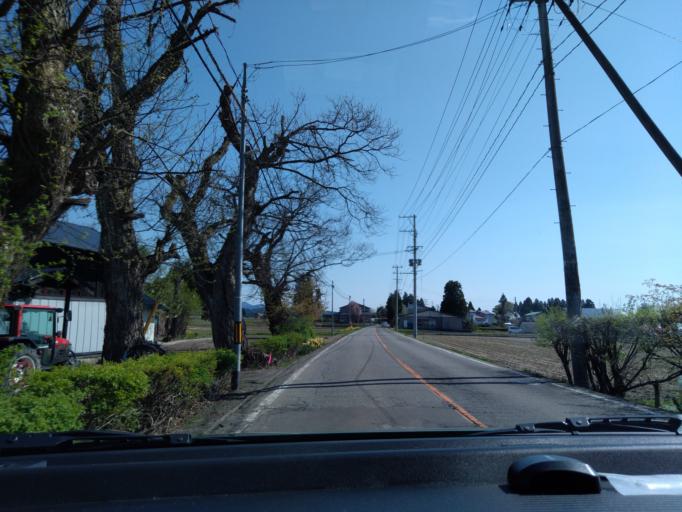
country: JP
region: Akita
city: Kakunodatemachi
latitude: 39.4931
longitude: 140.5941
